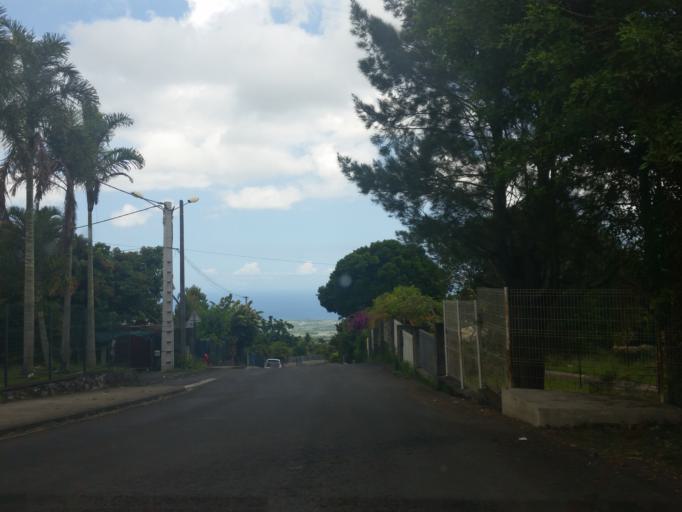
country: RE
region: Reunion
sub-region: Reunion
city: Le Tampon
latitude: -21.2538
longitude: 55.4980
